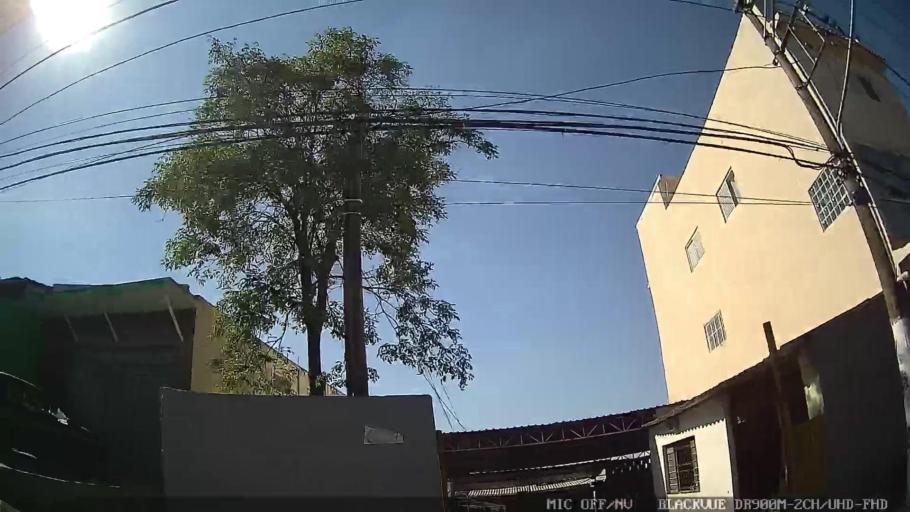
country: BR
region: Sao Paulo
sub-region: Ferraz De Vasconcelos
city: Ferraz de Vasconcelos
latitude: -23.5516
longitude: -46.4664
